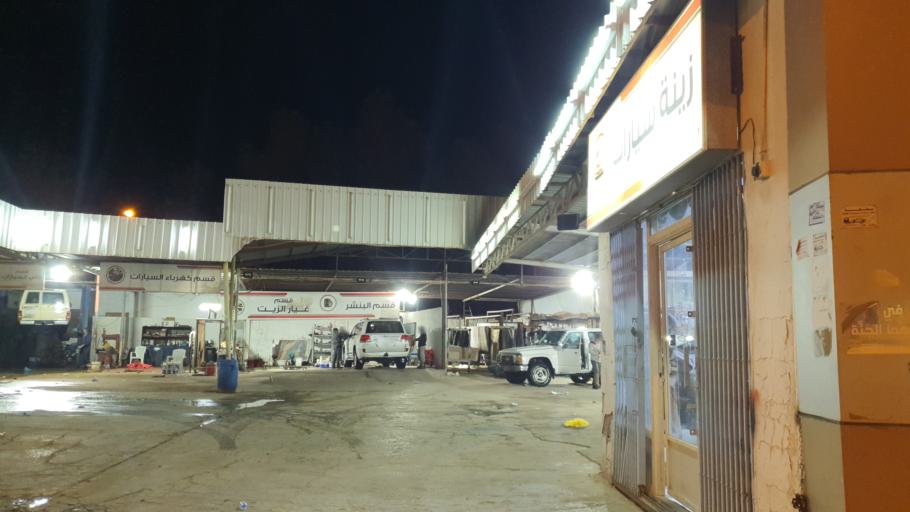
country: SA
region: Ar Riyad
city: Az Zulfi
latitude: 26.2930
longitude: 44.7966
